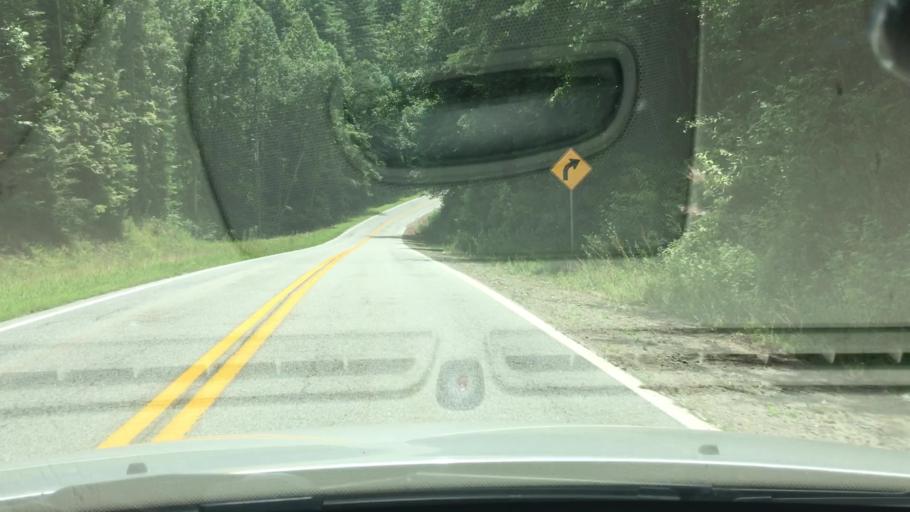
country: US
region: Georgia
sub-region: Lumpkin County
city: Dahlonega
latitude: 34.5753
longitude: -83.8889
